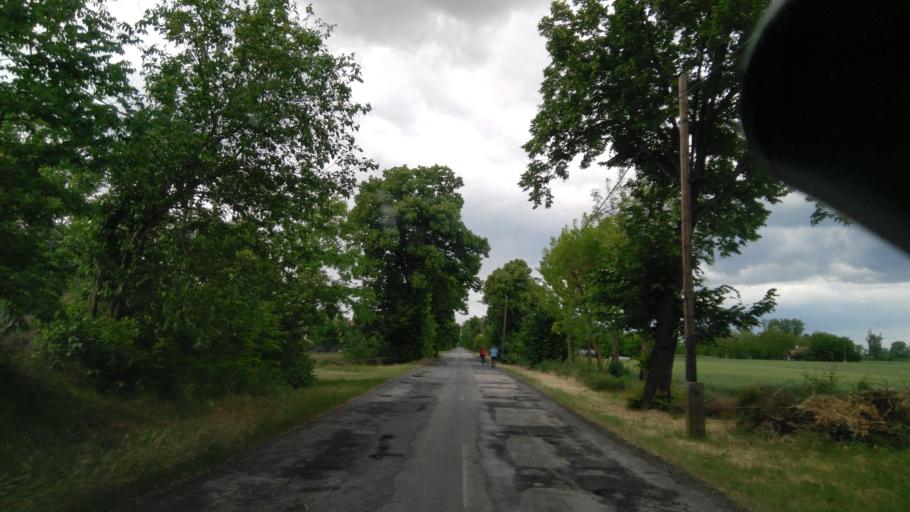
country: HU
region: Bekes
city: Gadoros
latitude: 46.6667
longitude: 20.5760
